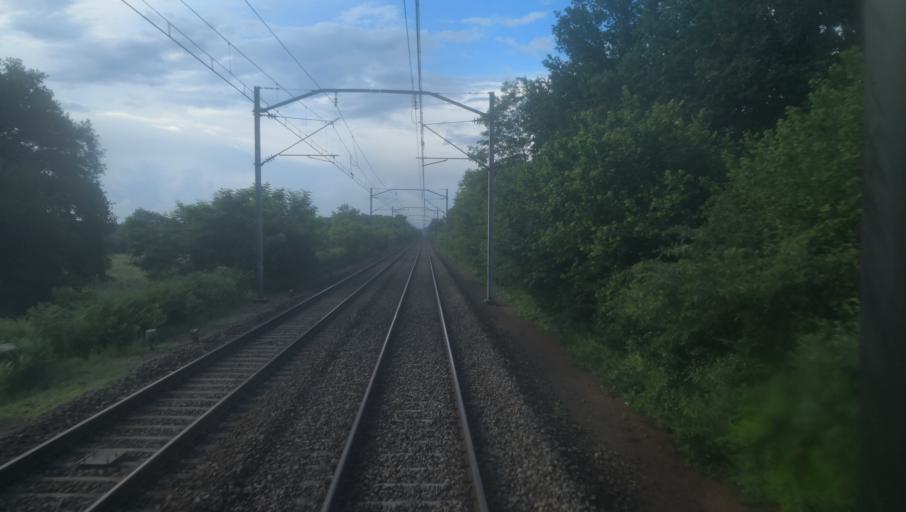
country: FR
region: Centre
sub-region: Departement du Loir-et-Cher
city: Nouan-le-Fuzelier
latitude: 47.5366
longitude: 2.0329
